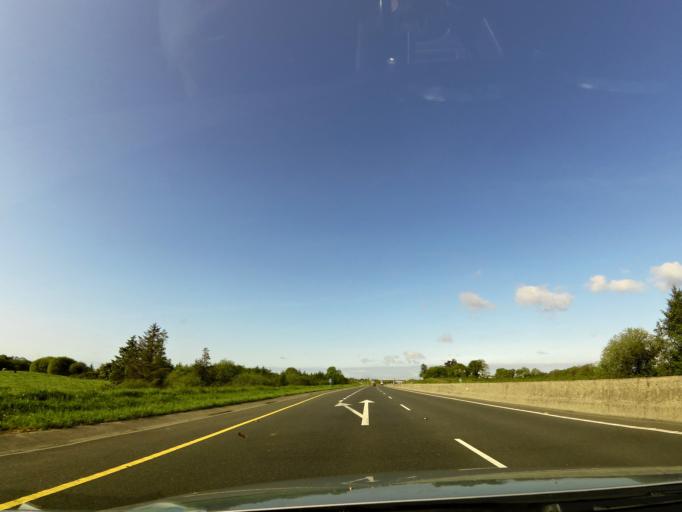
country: IE
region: Munster
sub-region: North Tipperary
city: Newport
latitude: 52.7601
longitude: -8.4010
